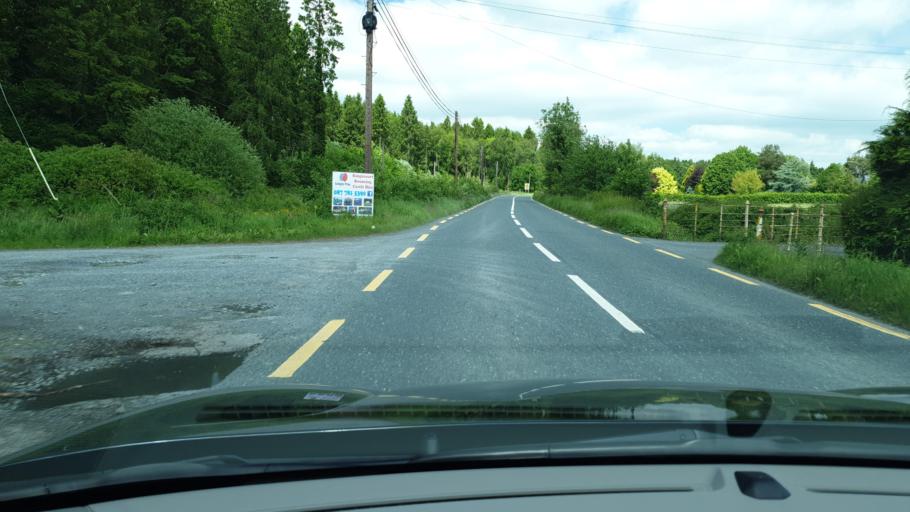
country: IE
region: Ulster
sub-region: An Cabhan
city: Kingscourt
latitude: 53.9095
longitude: -6.7879
